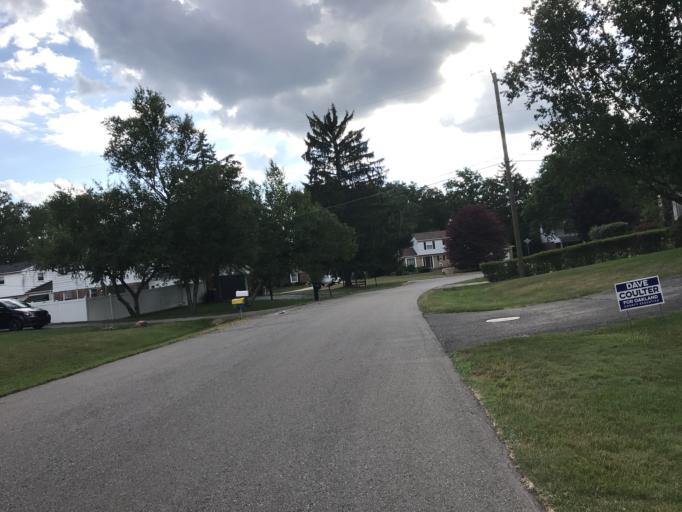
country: US
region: Michigan
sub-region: Oakland County
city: Farmington Hills
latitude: 42.4860
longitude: -83.3466
